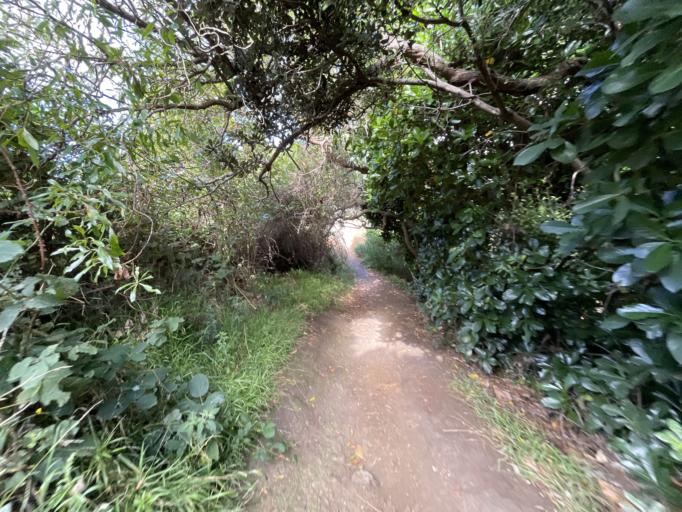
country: NZ
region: Wellington
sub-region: Wellington City
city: Wellington
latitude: -41.3047
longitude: 174.7871
